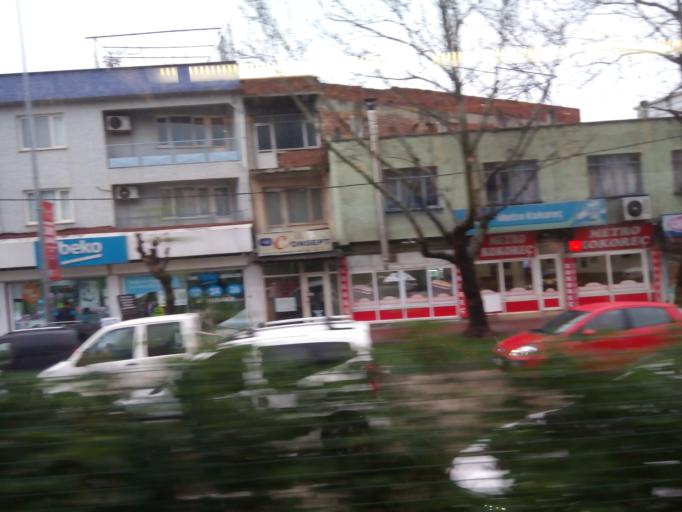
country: TR
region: Bursa
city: Yildirim
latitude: 40.2046
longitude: 29.0311
